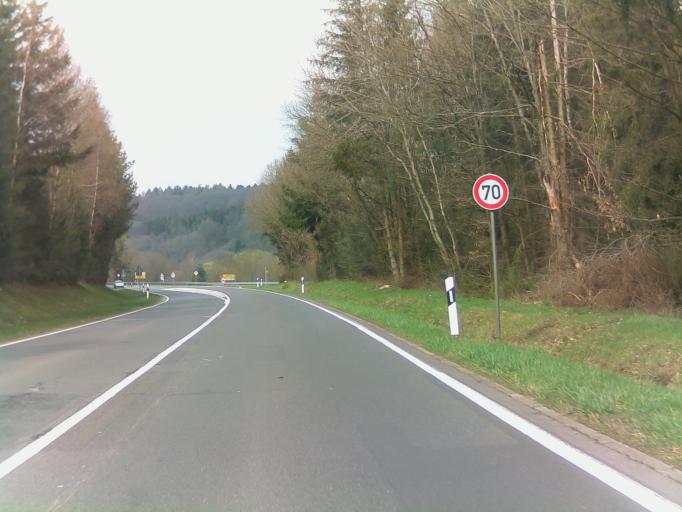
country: DE
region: Rheinland-Pfalz
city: Asbach
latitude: 49.8038
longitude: 7.2779
